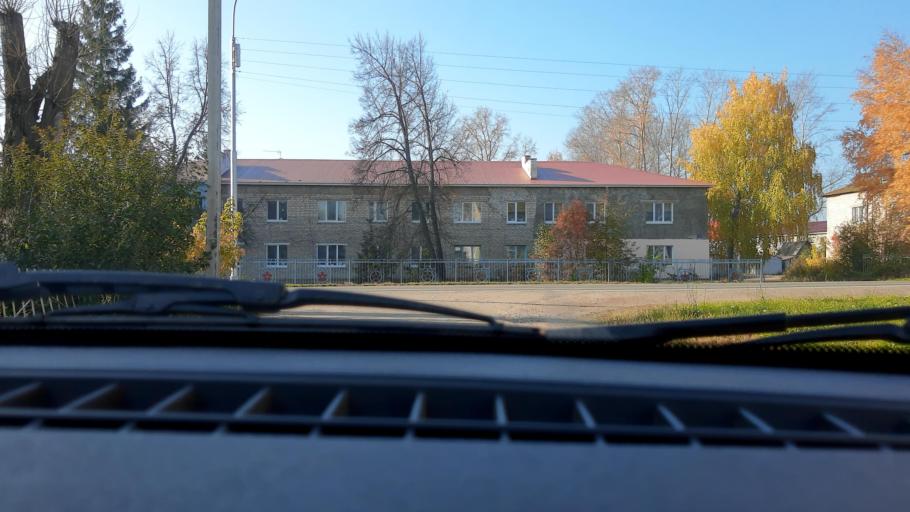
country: RU
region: Bashkortostan
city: Mikhaylovka
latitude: 54.8106
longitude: 55.8107
